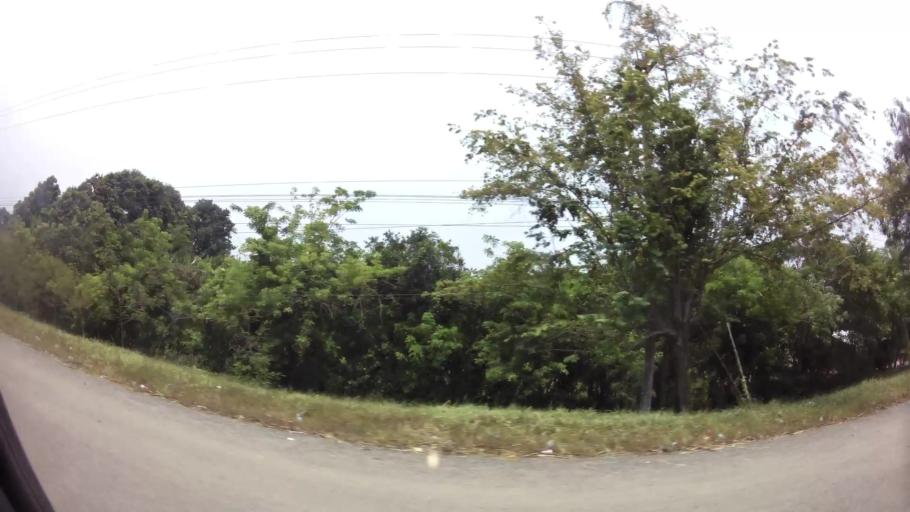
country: HN
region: Yoro
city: El Progreso
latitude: 15.4118
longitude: -87.8461
